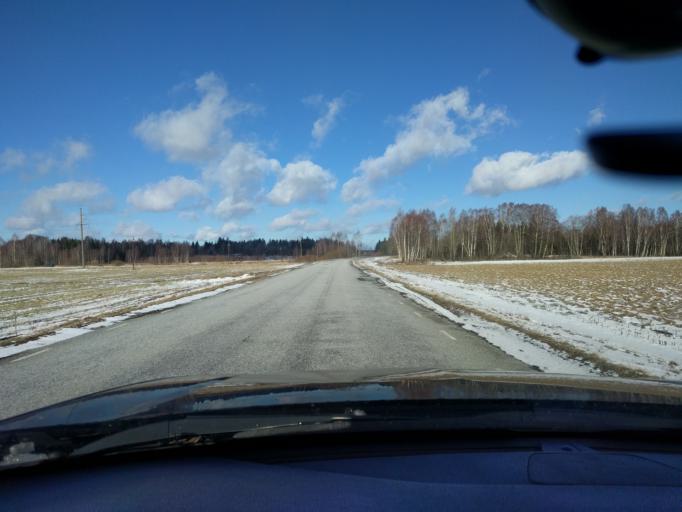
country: EE
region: Harju
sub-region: Raasiku vald
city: Raasiku
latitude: 59.3131
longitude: 25.1618
